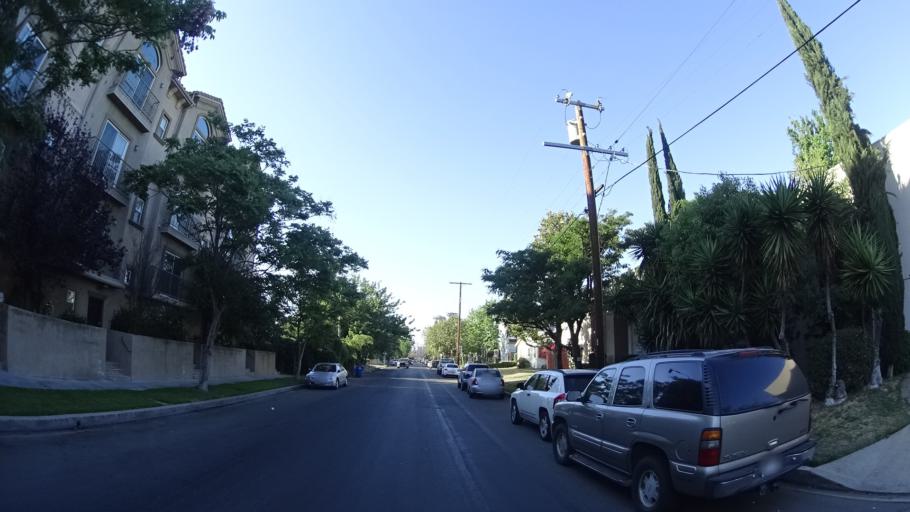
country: US
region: California
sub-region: Los Angeles County
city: North Hollywood
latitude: 34.1619
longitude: -118.3660
